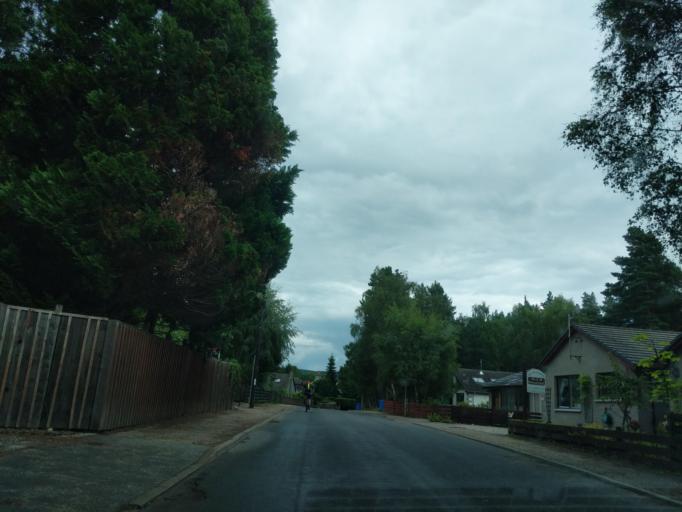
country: GB
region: Scotland
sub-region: Highland
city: Aviemore
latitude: 57.2816
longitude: -3.8283
